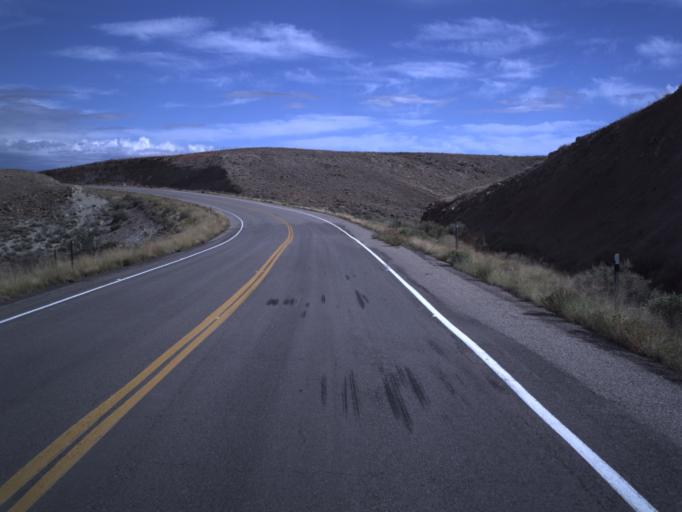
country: US
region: Colorado
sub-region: Montezuma County
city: Towaoc
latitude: 37.1732
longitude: -109.0993
